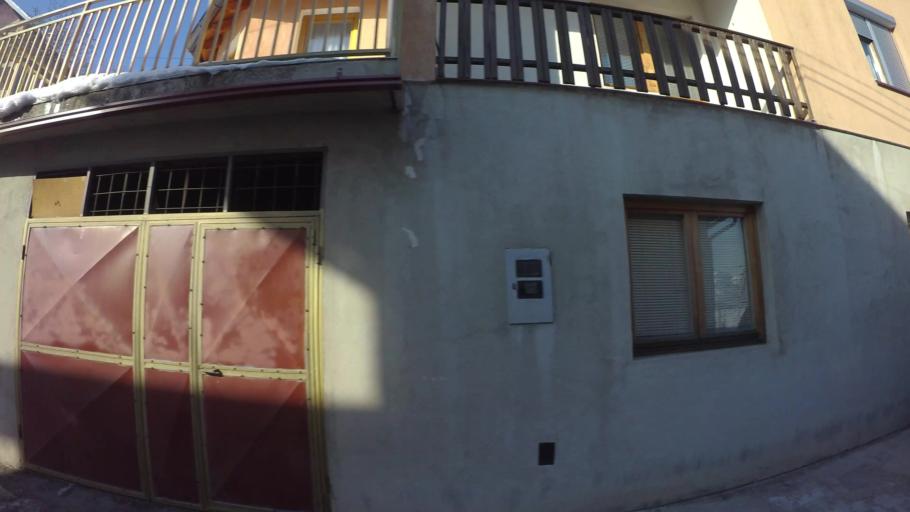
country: BA
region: Federation of Bosnia and Herzegovina
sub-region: Kanton Sarajevo
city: Sarajevo
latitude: 43.8374
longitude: 18.3639
